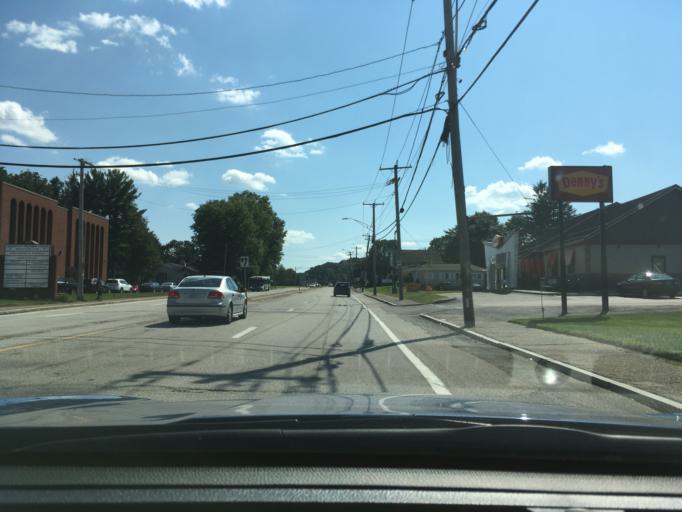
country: US
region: Rhode Island
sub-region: Providence County
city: Cranston
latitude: 41.7699
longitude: -71.4547
